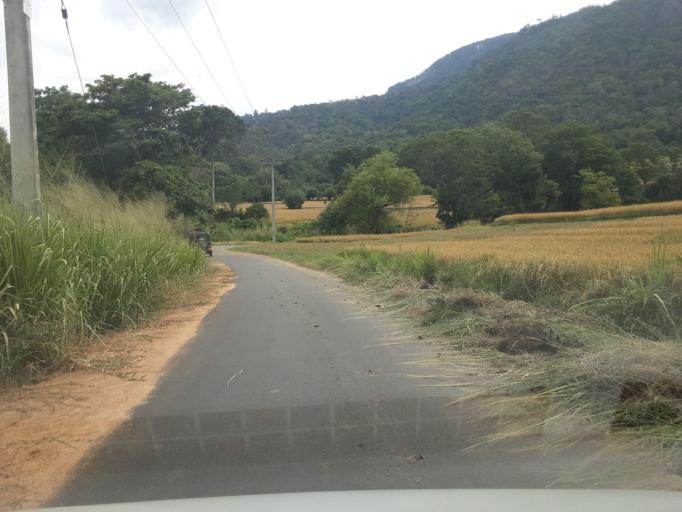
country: LK
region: Uva
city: Badulla
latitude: 7.0893
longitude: 80.9375
